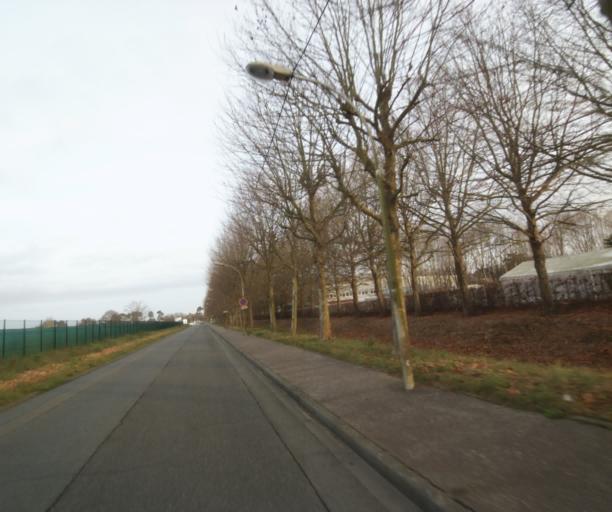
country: FR
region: Pays de la Loire
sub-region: Departement de la Sarthe
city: Arnage
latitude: 47.9427
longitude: 0.2138
